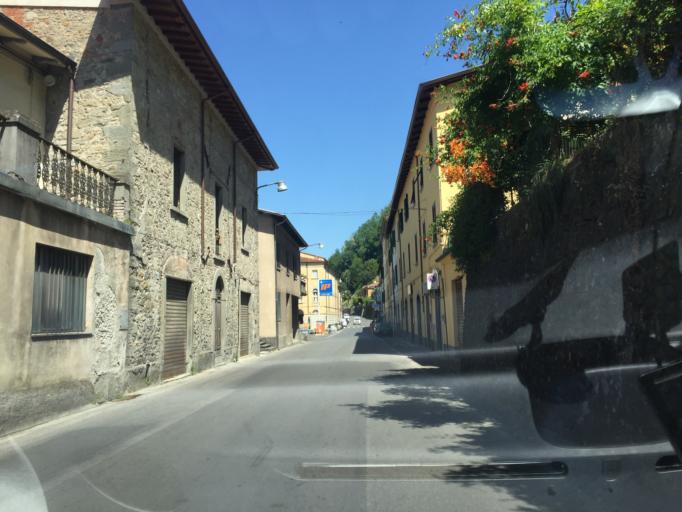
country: IT
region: Tuscany
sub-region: Provincia di Lucca
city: Castelnuovo di Garfagnana
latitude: 44.1114
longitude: 10.4133
